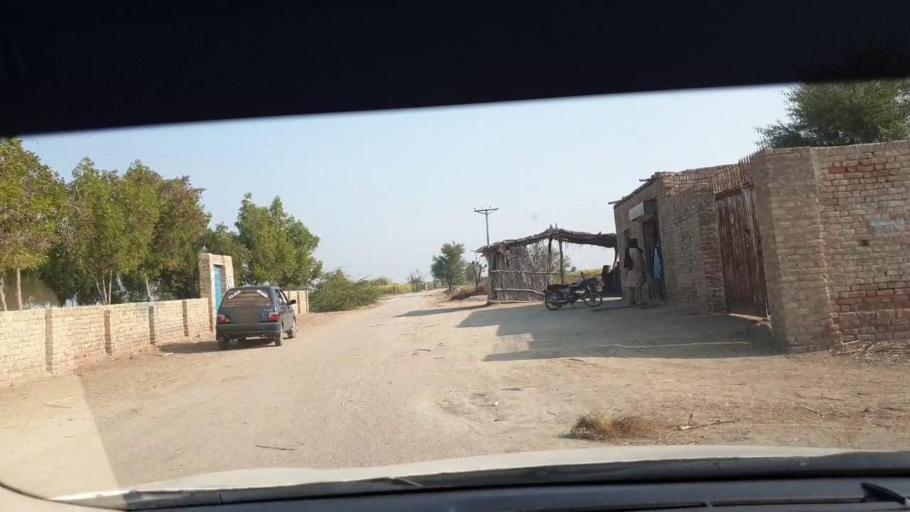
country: PK
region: Sindh
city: Berani
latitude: 25.8211
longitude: 68.7703
